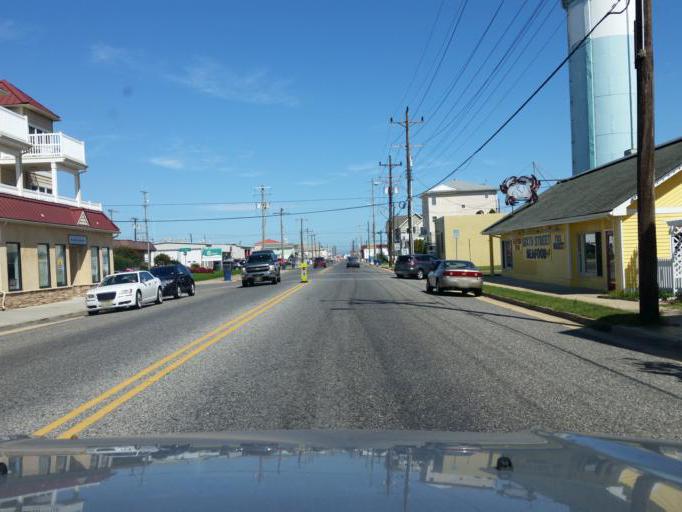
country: US
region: New Jersey
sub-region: Cape May County
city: North Wildwood
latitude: 39.0047
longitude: -74.7975
